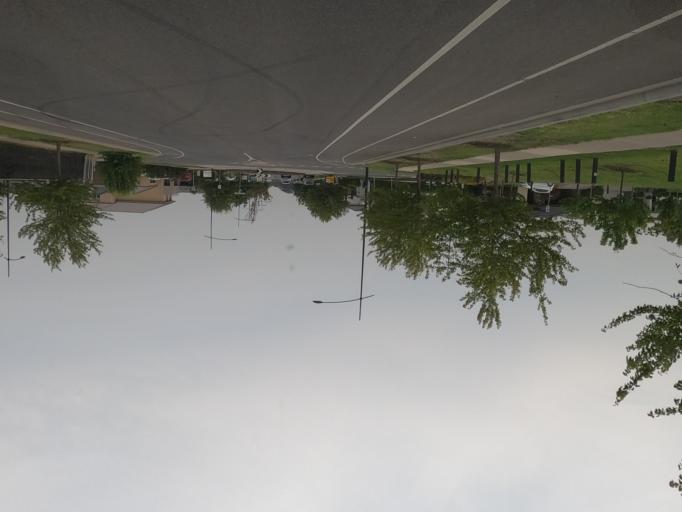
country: AU
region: Victoria
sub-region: Hume
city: Greenvale
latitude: -37.6228
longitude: 144.8786
